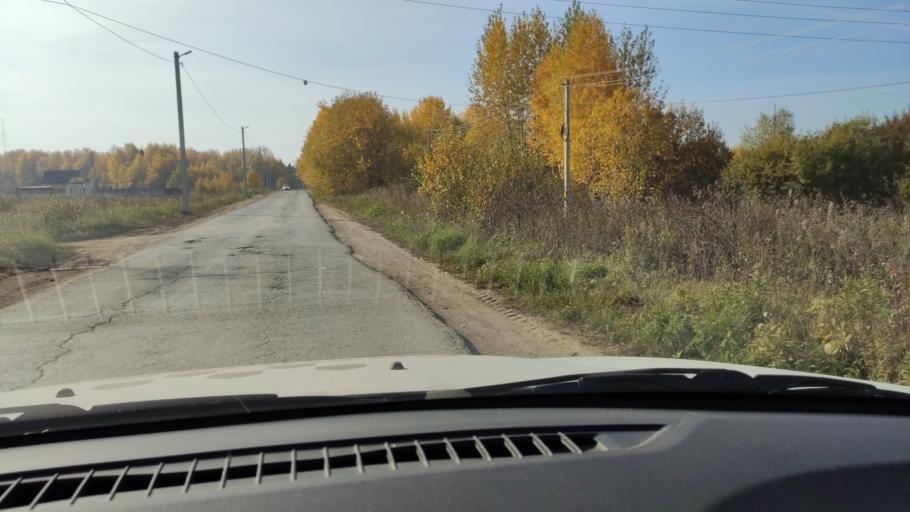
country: RU
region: Perm
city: Sylva
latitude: 58.0370
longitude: 56.7421
